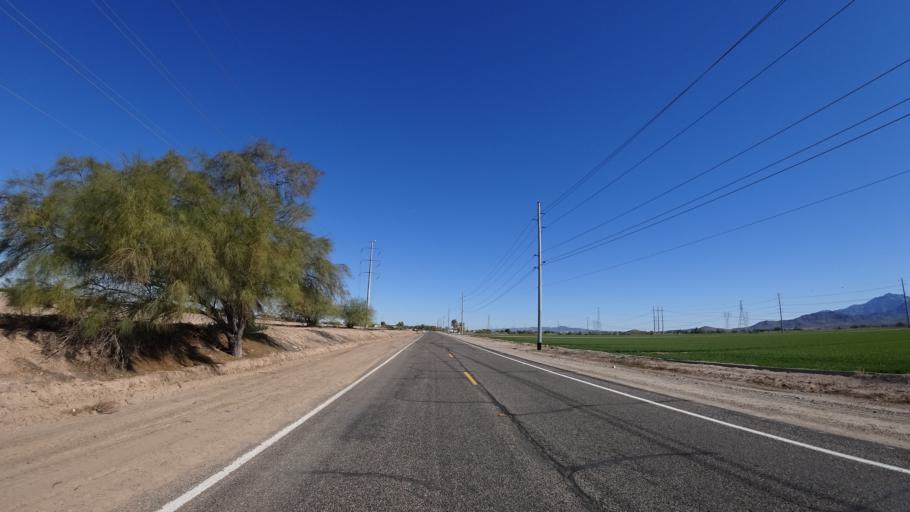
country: US
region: Arizona
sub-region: Maricopa County
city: Goodyear
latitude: 33.4064
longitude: -112.3637
